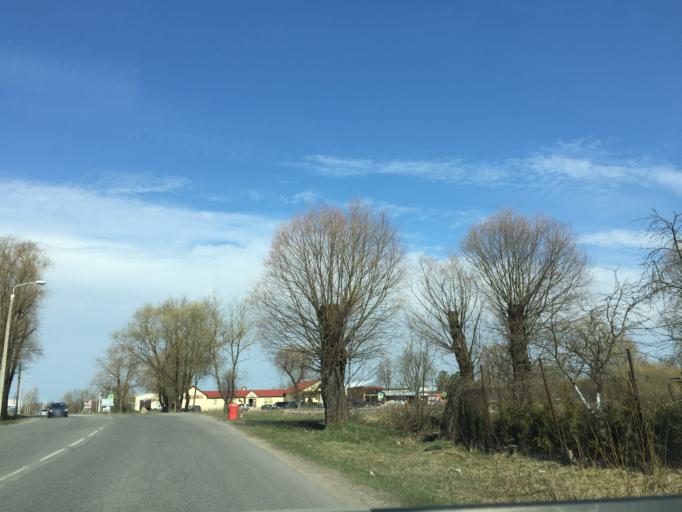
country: EE
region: Ida-Virumaa
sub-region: Narva linn
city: Narva
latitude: 59.3867
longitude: 28.1890
